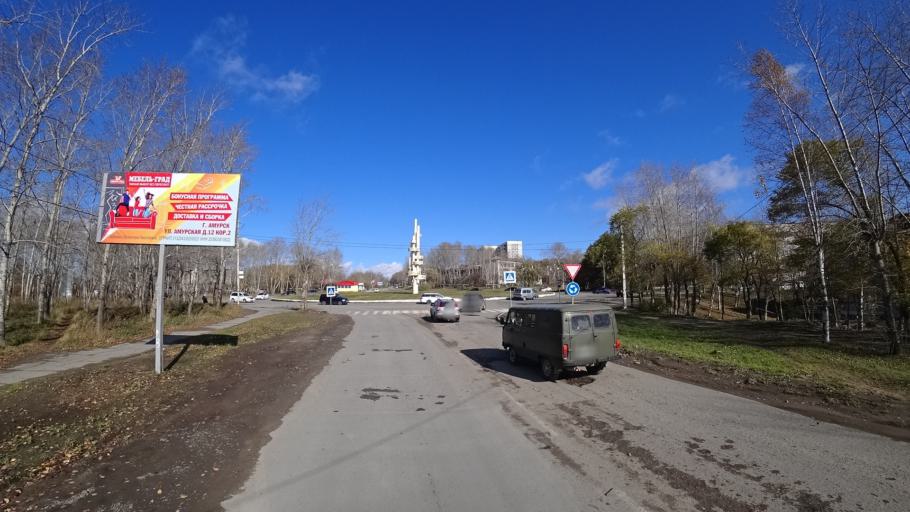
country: RU
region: Khabarovsk Krai
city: Amursk
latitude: 50.2292
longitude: 136.9014
